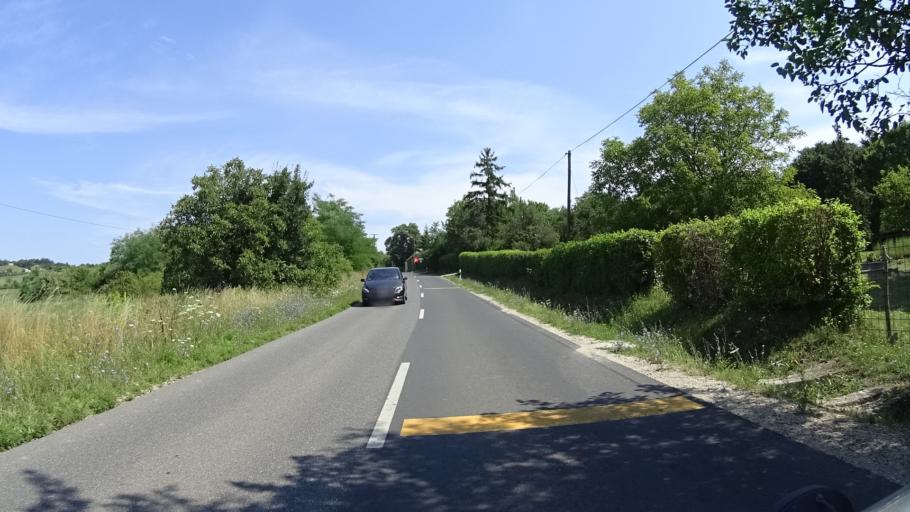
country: HU
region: Veszprem
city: Zanka
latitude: 46.9351
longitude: 17.6892
